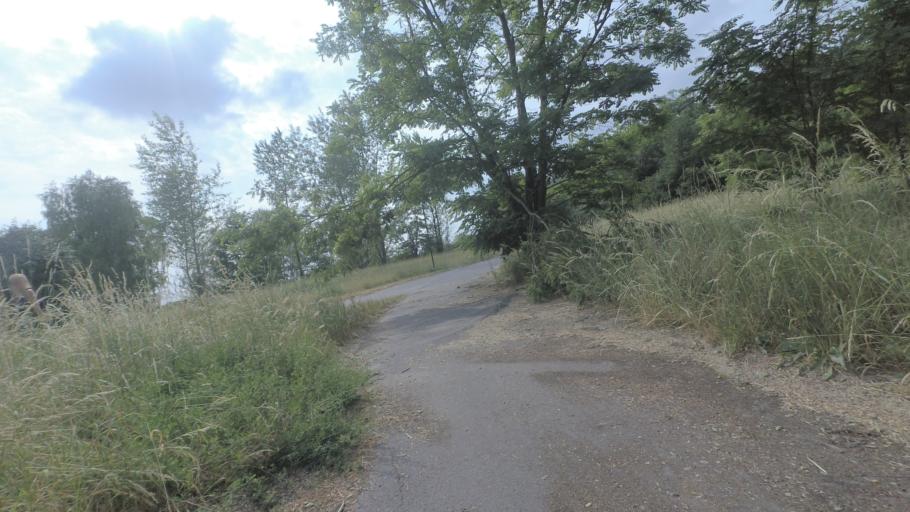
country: DE
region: Berlin
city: Rudow
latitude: 52.4041
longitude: 13.4769
